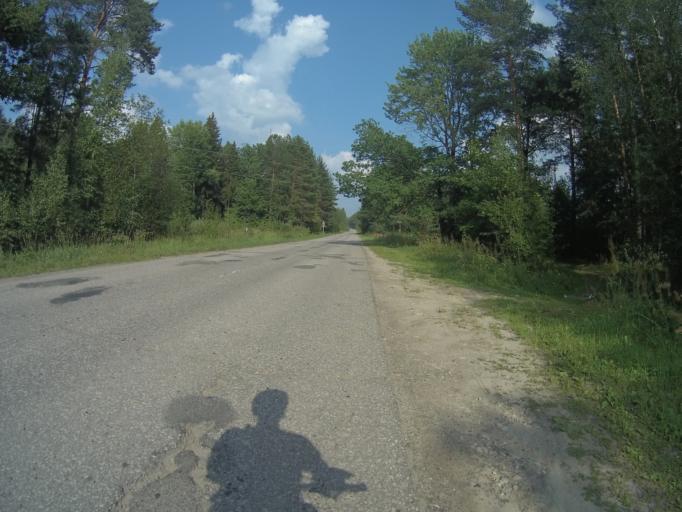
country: RU
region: Vladimir
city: Kommunar
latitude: 56.0682
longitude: 40.5038
